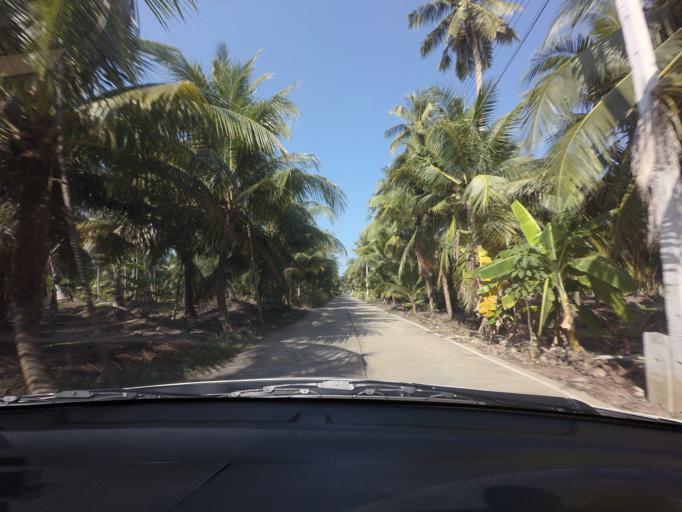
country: TH
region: Samut Songkhram
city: Bang Khon Thi
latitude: 13.4718
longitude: 99.9733
